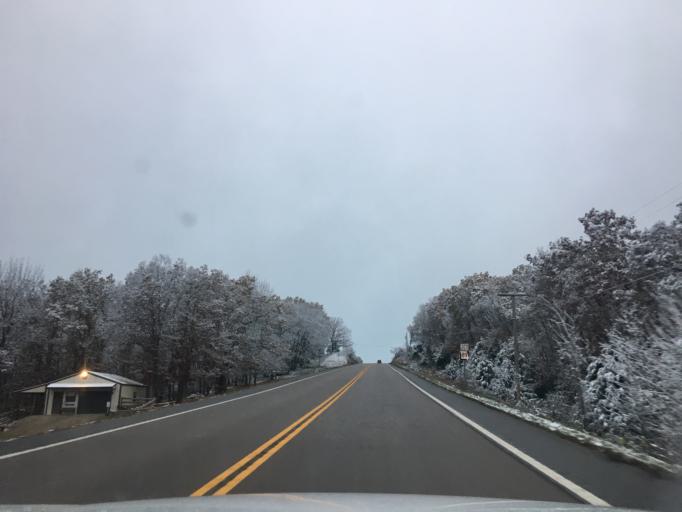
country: US
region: Missouri
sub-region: Osage County
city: Linn
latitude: 38.4724
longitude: -91.7815
